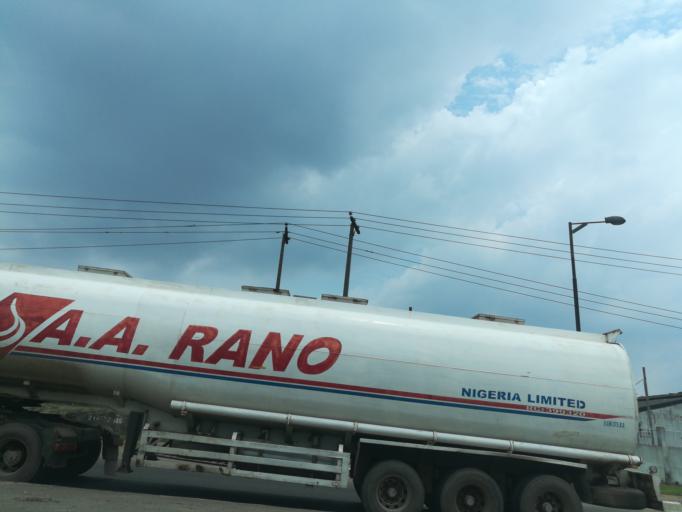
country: NG
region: Lagos
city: Ojota
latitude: 6.5854
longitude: 3.3772
